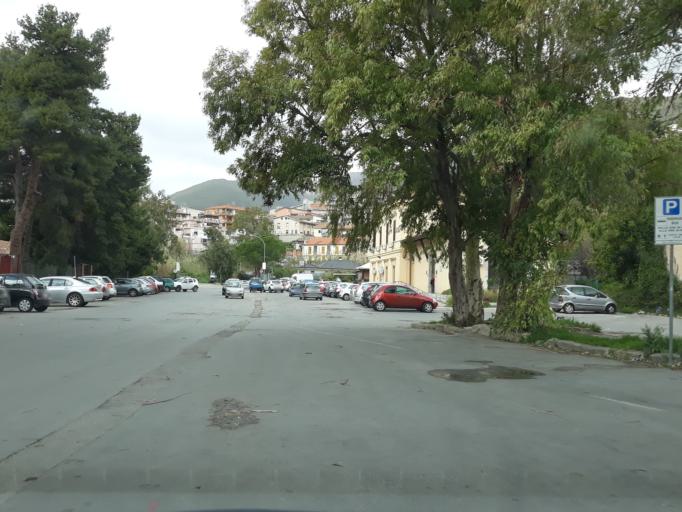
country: IT
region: Sicily
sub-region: Palermo
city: Monreale
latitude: 38.0772
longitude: 13.2898
